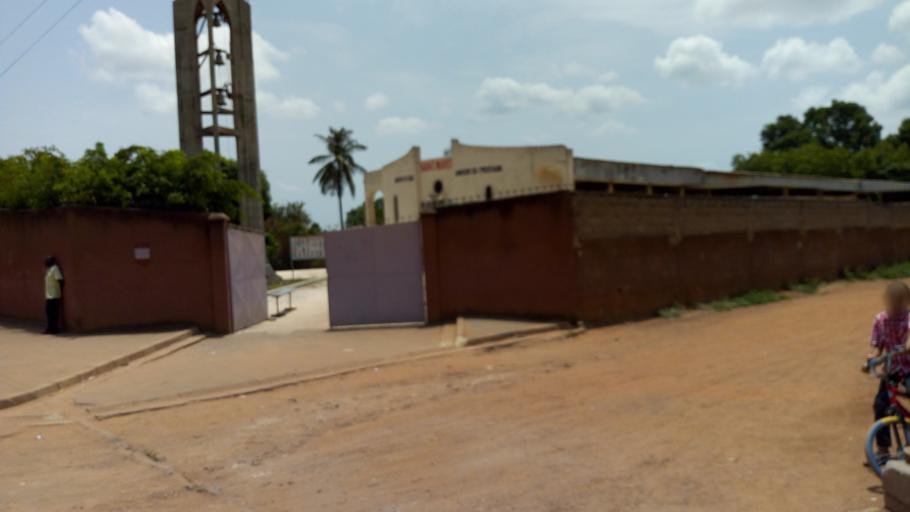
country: CI
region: Vallee du Bandama
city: Bouake
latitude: 7.6712
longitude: -5.0139
